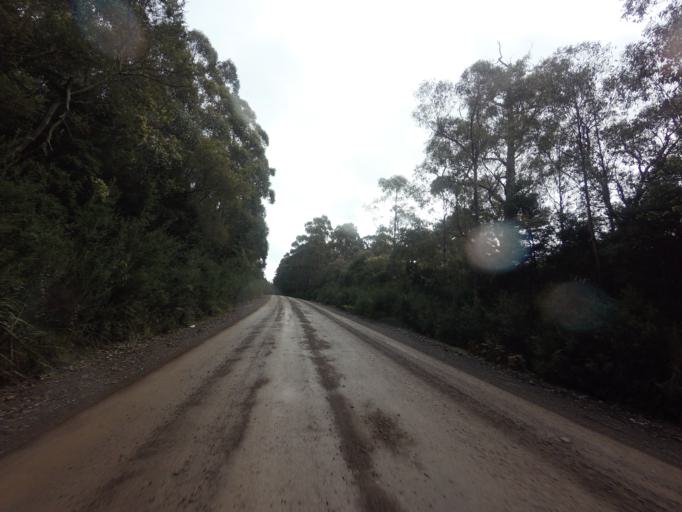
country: AU
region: Tasmania
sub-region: Huon Valley
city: Geeveston
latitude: -43.4650
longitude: 146.8998
